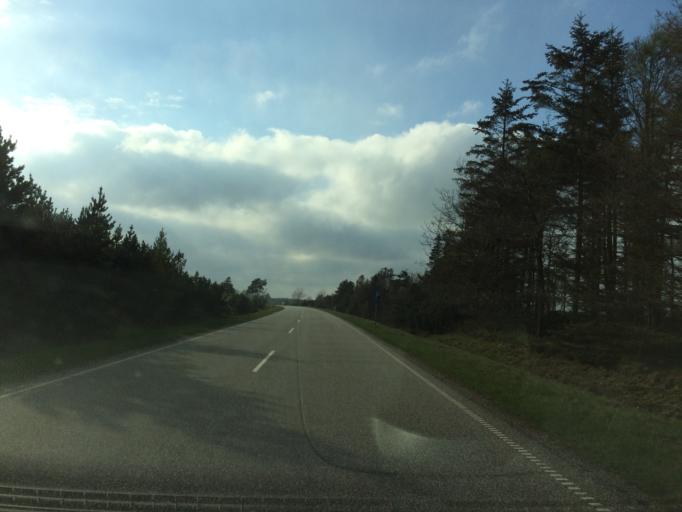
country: DK
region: Central Jutland
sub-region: Viborg Kommune
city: Karup
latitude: 56.3365
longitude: 9.0901
